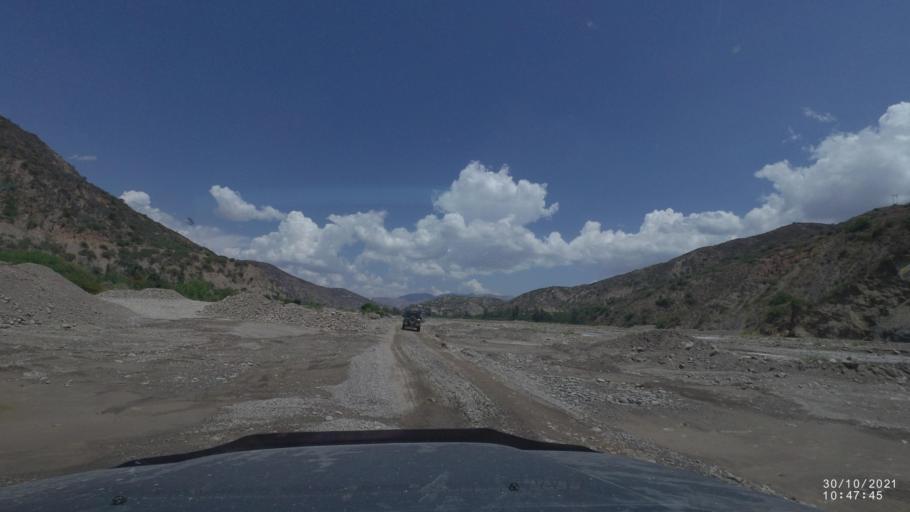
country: BO
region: Cochabamba
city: Sipe Sipe
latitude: -17.5595
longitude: -66.4615
